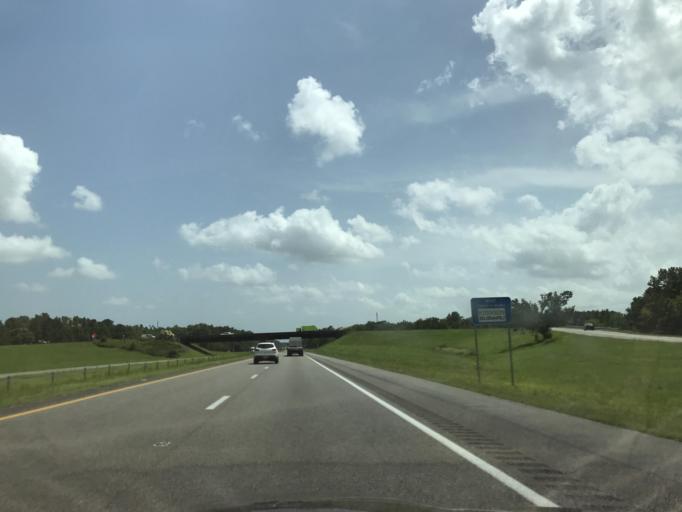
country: US
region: North Carolina
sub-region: Pender County
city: Rocky Point
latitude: 34.4432
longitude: -77.8751
